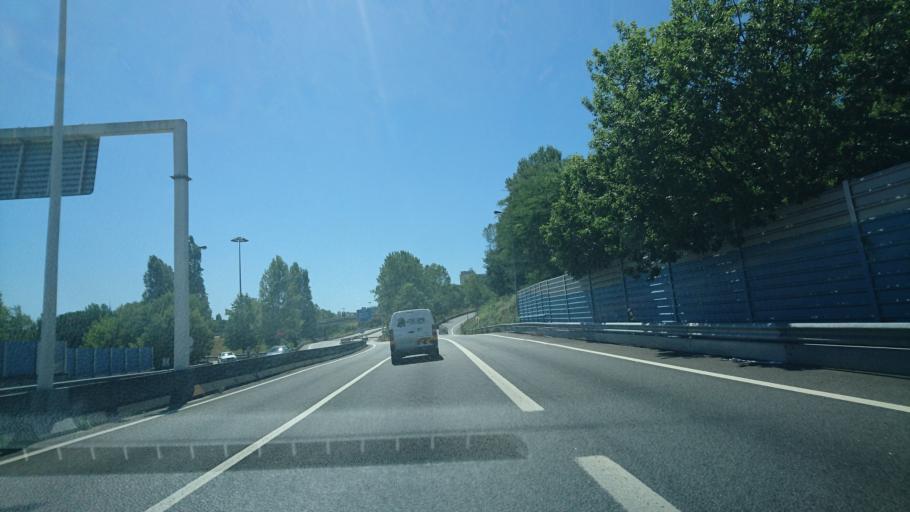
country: PT
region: Porto
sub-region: Gondomar
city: Valbom
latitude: 41.1523
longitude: -8.5745
